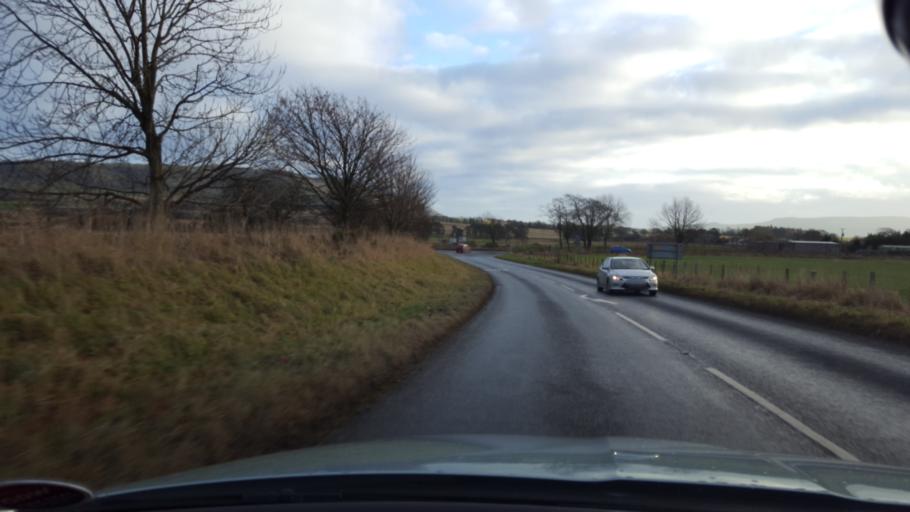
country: GB
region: Scotland
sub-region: Perth and Kinross
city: Milnathort
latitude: 56.2473
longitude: -3.3733
